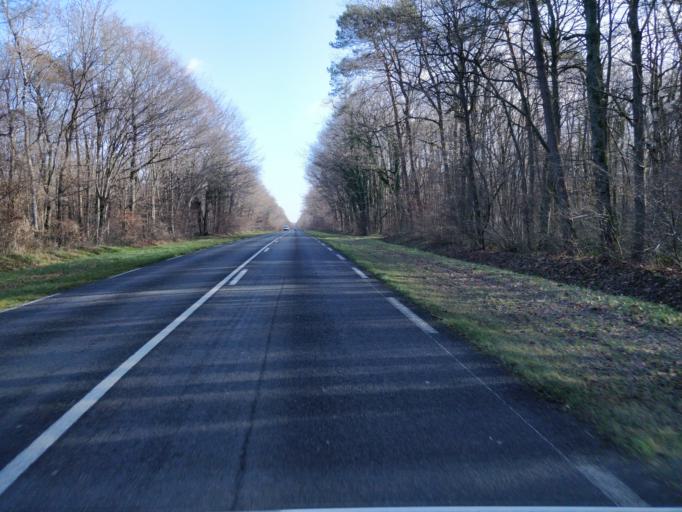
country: FR
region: Ile-de-France
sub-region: Departement de Seine-et-Marne
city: Bagneaux-sur-Loing
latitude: 48.2448
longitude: 2.7848
